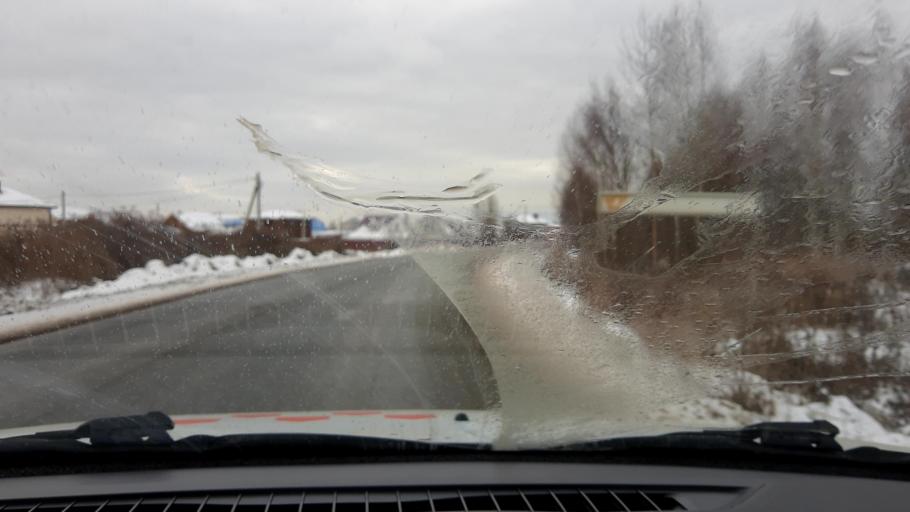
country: RU
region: Nizjnij Novgorod
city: Neklyudovo
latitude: 56.4265
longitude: 43.9637
